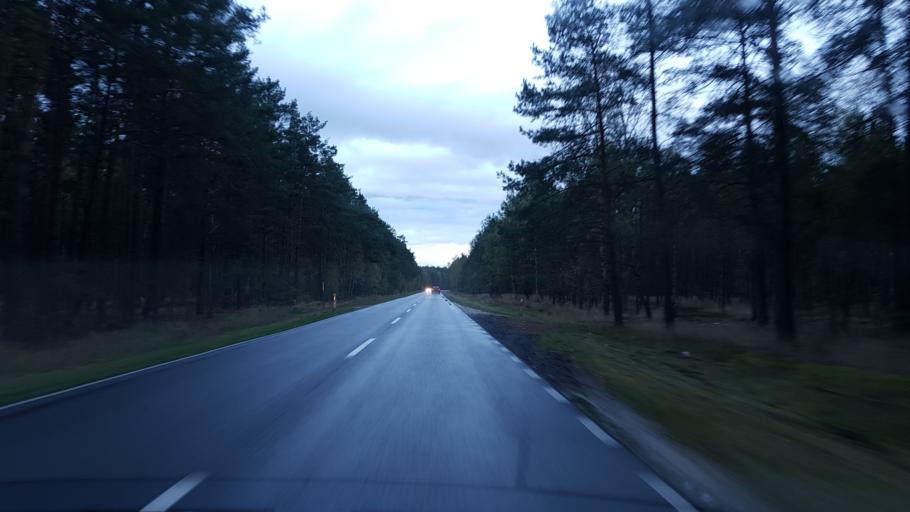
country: PL
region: Greater Poland Voivodeship
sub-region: Powiat pilski
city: Pila
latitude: 53.1947
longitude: 16.8249
